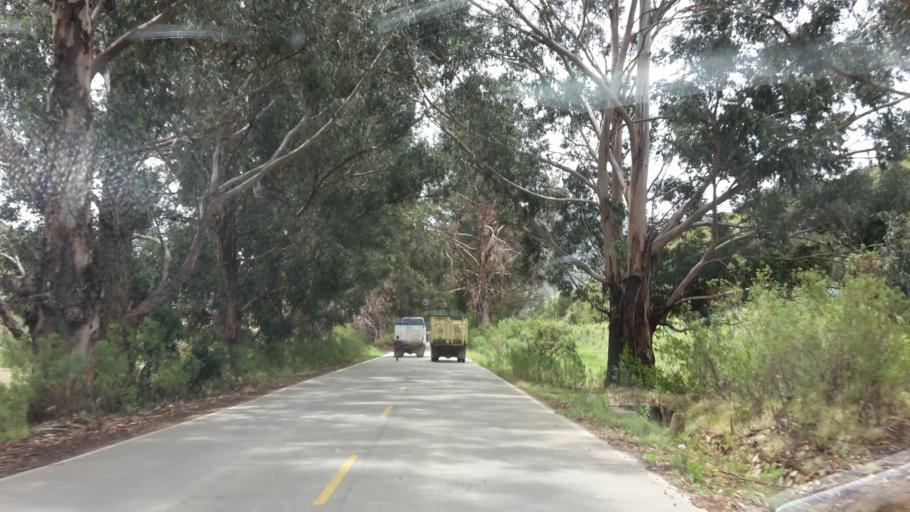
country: BO
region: Cochabamba
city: Totora
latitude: -17.6508
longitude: -65.2289
